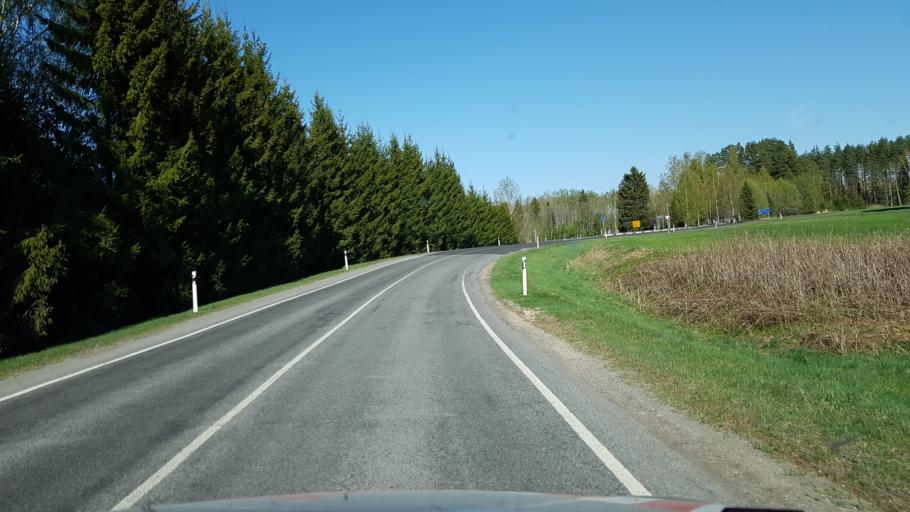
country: EE
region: Viljandimaa
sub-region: Viljandi linn
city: Viljandi
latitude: 58.3215
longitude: 25.5718
